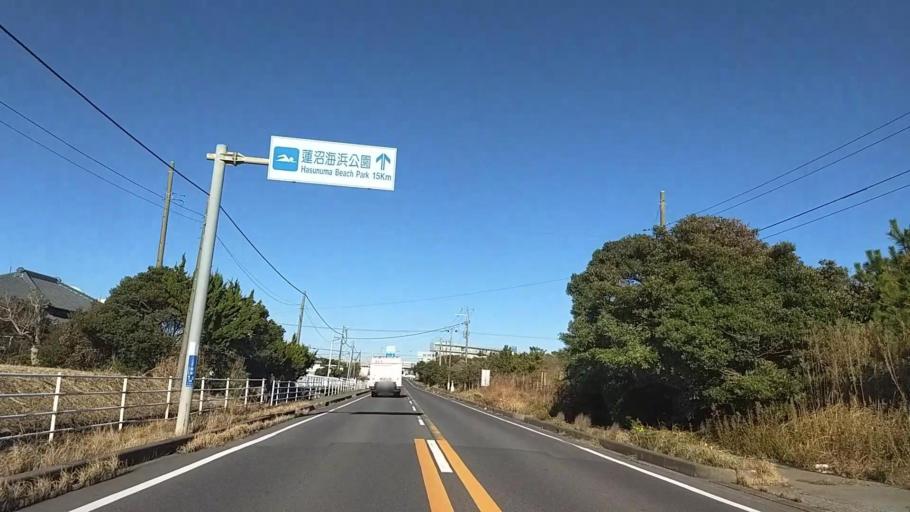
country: JP
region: Chiba
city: Togane
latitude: 35.4969
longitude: 140.4268
